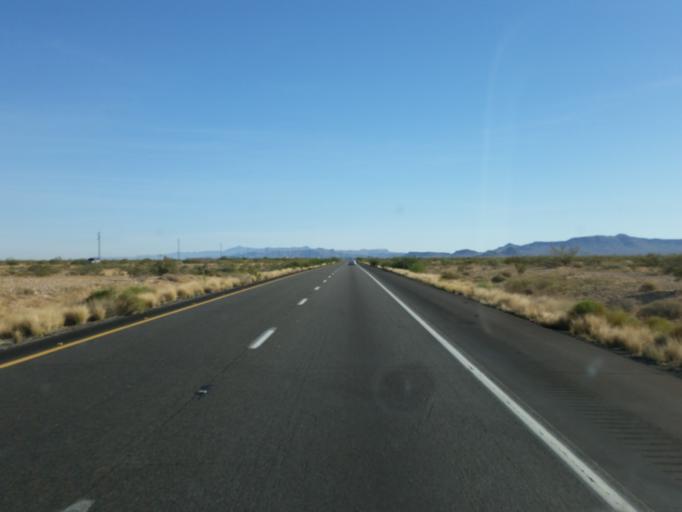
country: US
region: Arizona
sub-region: Mohave County
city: Kingman
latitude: 34.9868
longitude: -114.1388
